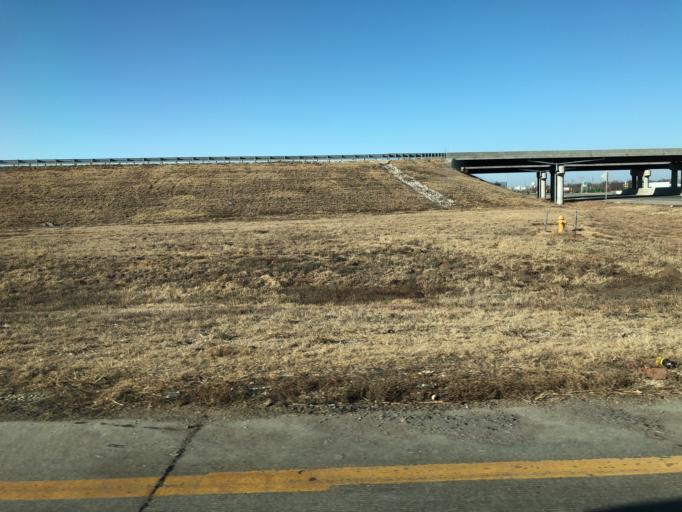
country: US
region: Kansas
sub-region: Reno County
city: South Hutchinson
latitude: 38.0267
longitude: -97.9041
